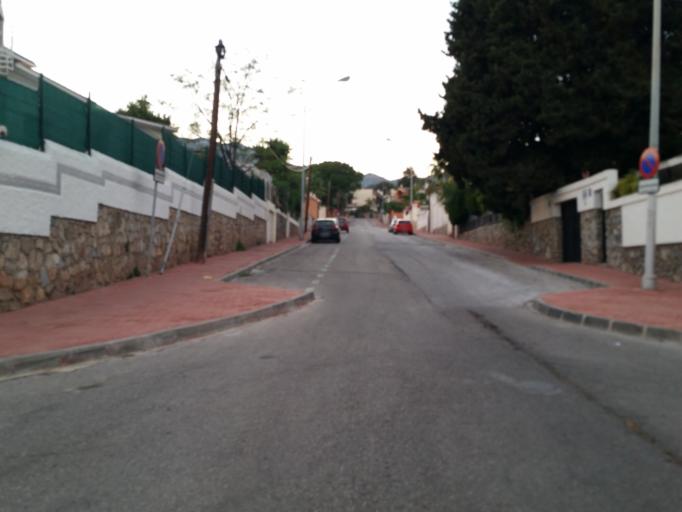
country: ES
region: Andalusia
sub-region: Provincia de Malaga
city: Torremolinos
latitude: 36.6005
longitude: -4.5194
